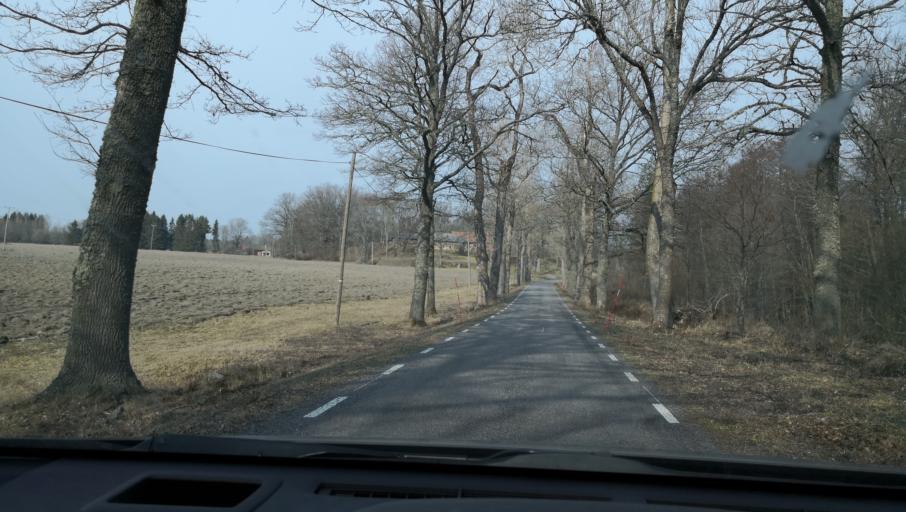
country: SE
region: OErebro
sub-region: Lindesbergs Kommun
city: Frovi
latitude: 59.4019
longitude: 15.4146
